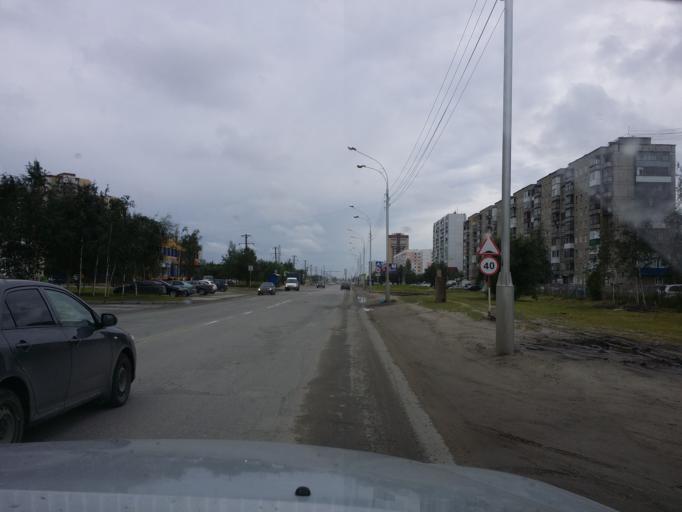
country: RU
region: Khanty-Mansiyskiy Avtonomnyy Okrug
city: Nizhnevartovsk
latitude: 60.9328
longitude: 76.6107
